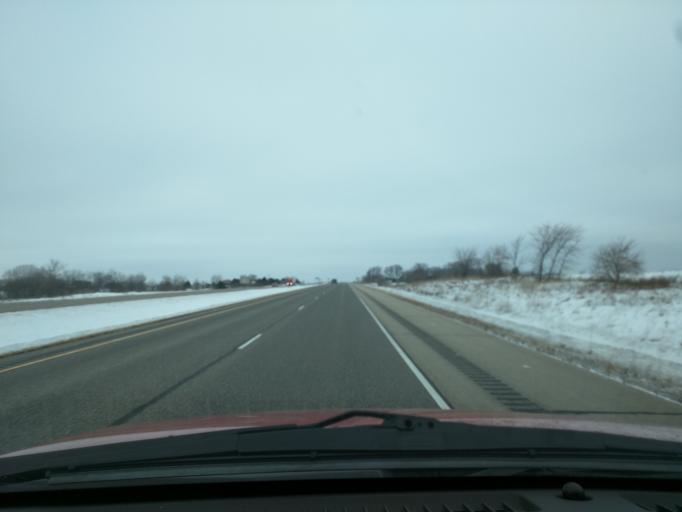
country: US
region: Minnesota
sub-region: Winona County
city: Winona
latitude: 43.9270
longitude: -91.6154
